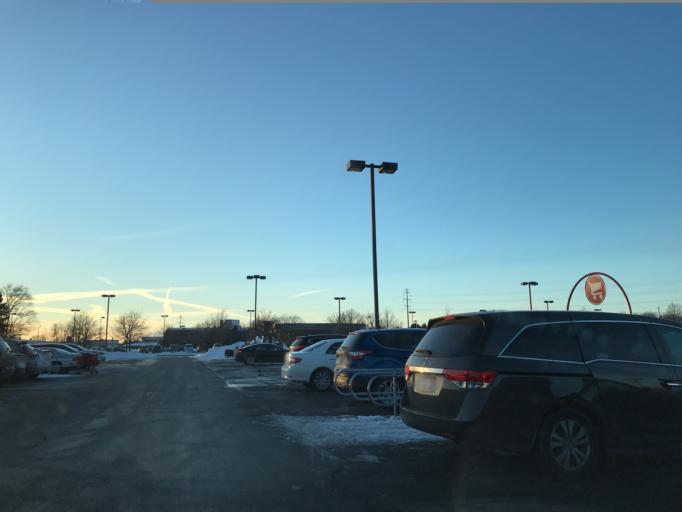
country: US
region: Michigan
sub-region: Washtenaw County
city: Ypsilanti
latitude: 42.2355
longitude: -83.6779
